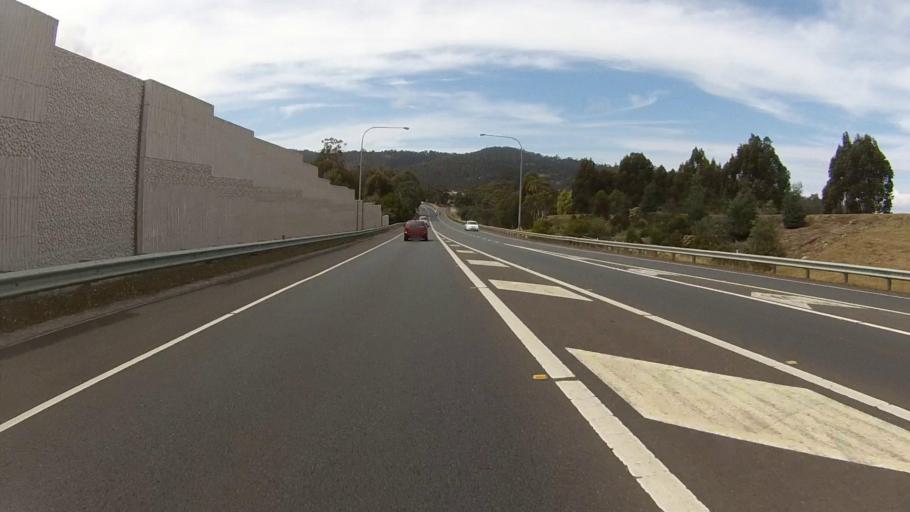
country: AU
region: Tasmania
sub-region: Kingborough
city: Kingston
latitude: -42.9735
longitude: 147.3050
